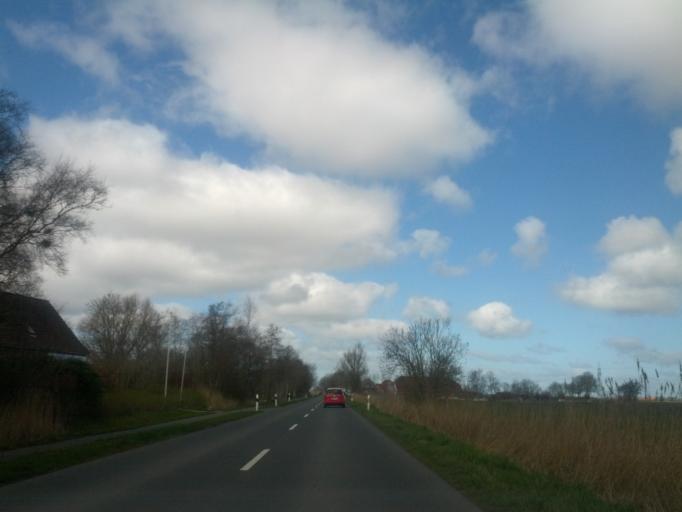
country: DE
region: Lower Saxony
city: Esens
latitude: 53.6597
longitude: 7.6046
